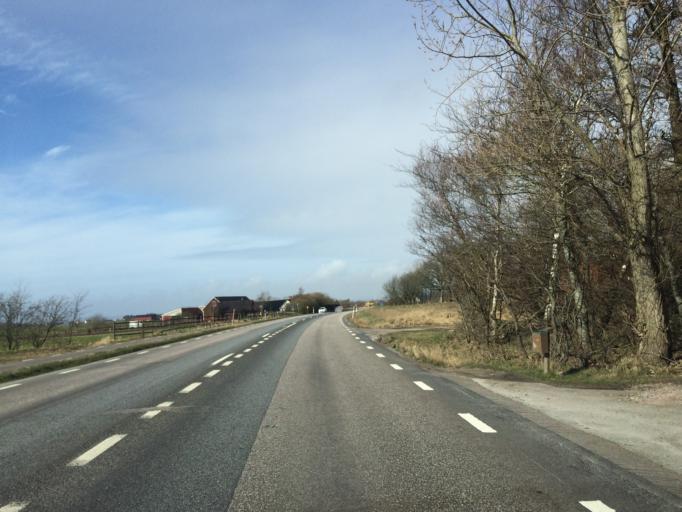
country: SE
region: Halland
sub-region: Halmstads Kommun
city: Paarp
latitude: 56.6043
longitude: 12.9617
